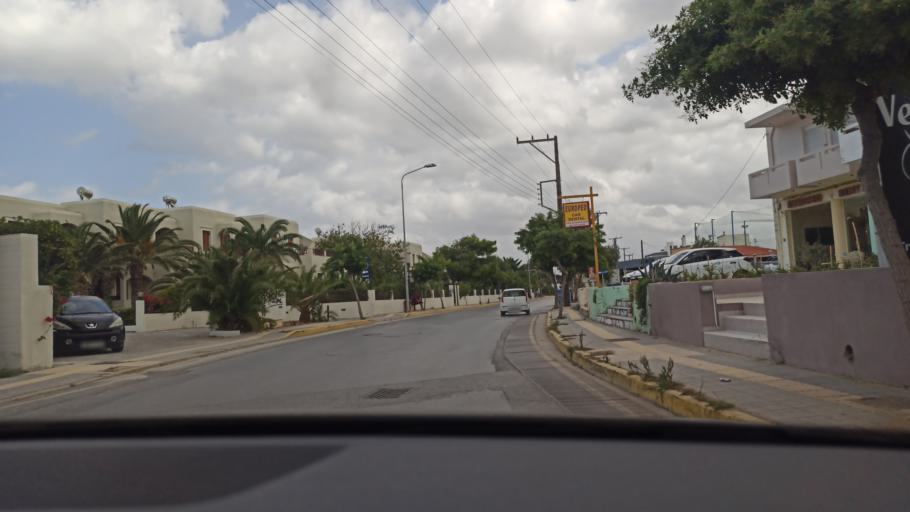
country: GR
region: Crete
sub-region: Nomos Irakleiou
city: Gazi
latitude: 35.3350
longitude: 25.0918
